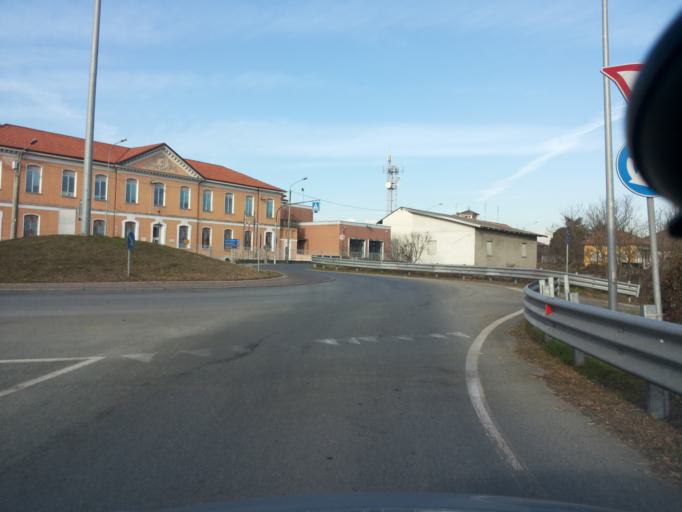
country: IT
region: Piedmont
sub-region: Provincia di Vercelli
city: Arborio
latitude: 45.4988
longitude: 8.3901
